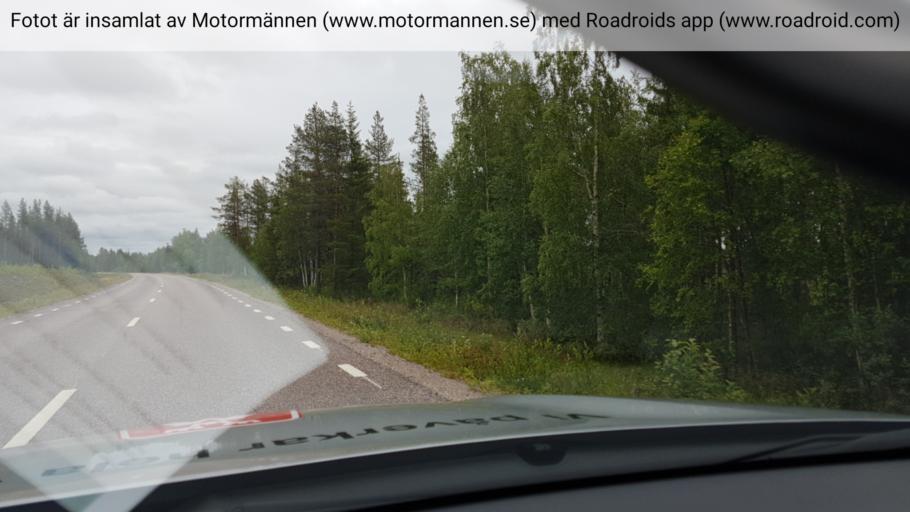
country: SE
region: Norrbotten
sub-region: Gallivare Kommun
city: Gaellivare
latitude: 67.0740
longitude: 21.3839
